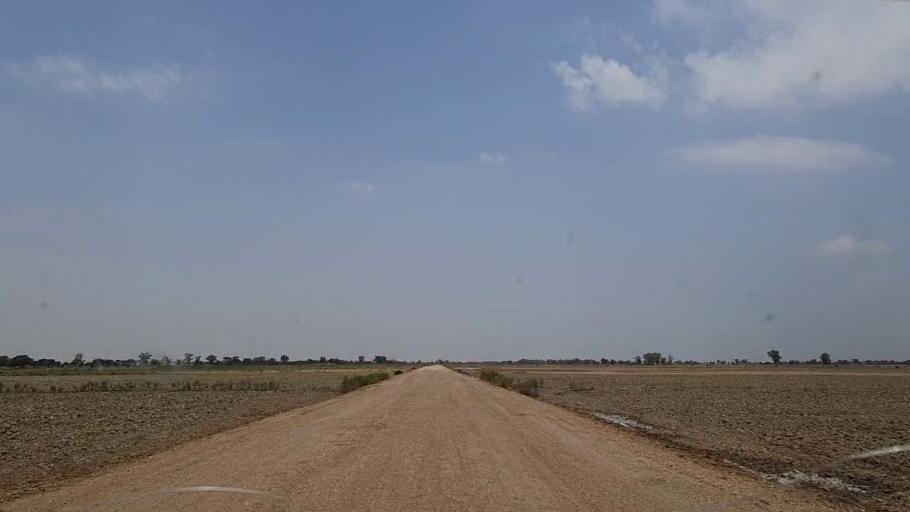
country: PK
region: Sindh
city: Phulji
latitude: 26.8100
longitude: 67.6340
